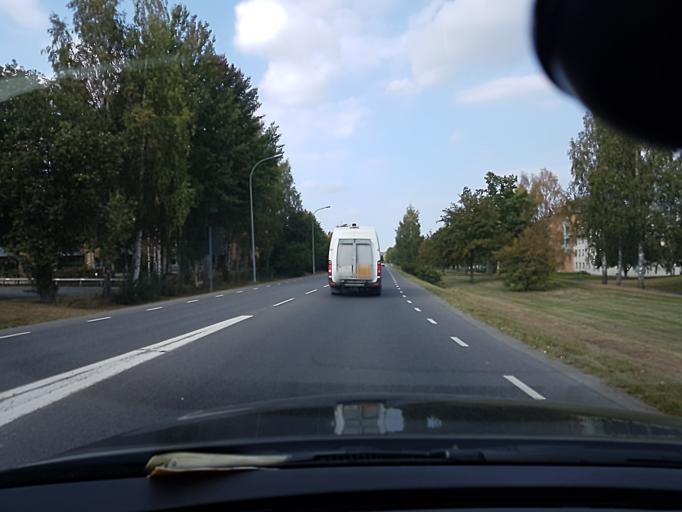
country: SE
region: Kronoberg
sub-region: Vaxjo Kommun
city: Vaexjoe
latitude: 56.8509
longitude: 14.8232
